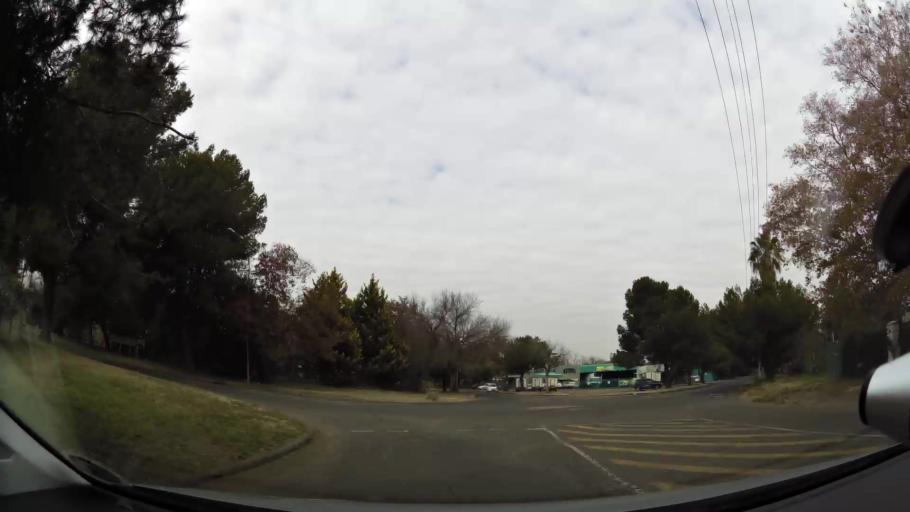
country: ZA
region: Orange Free State
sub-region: Mangaung Metropolitan Municipality
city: Bloemfontein
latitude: -29.1207
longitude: 26.1969
